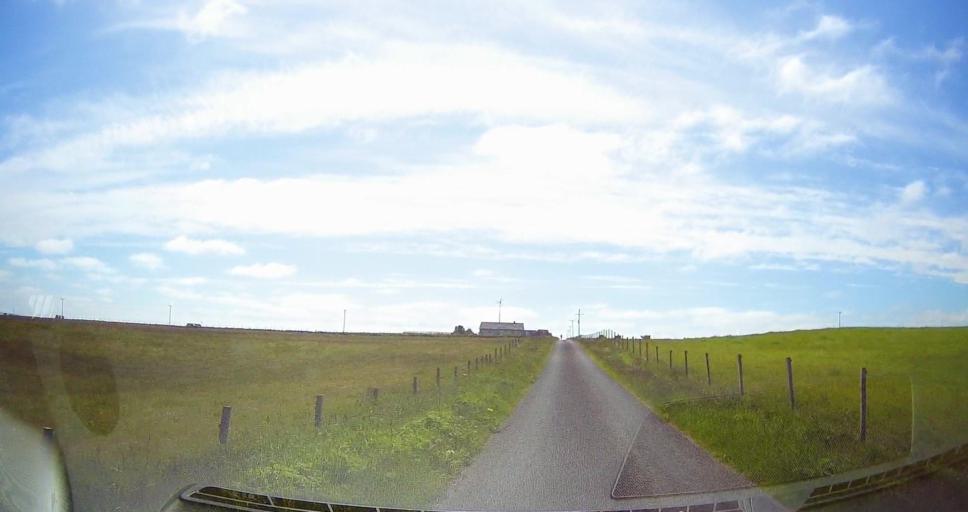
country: GB
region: Scotland
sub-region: Orkney Islands
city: Kirkwall
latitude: 58.8334
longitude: -2.8999
